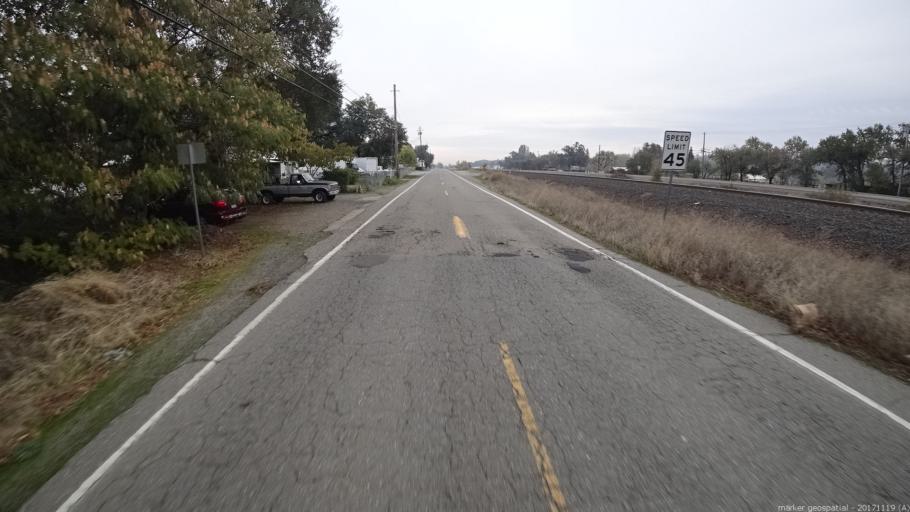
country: US
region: California
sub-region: Shasta County
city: Anderson
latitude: 40.4926
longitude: -122.3622
